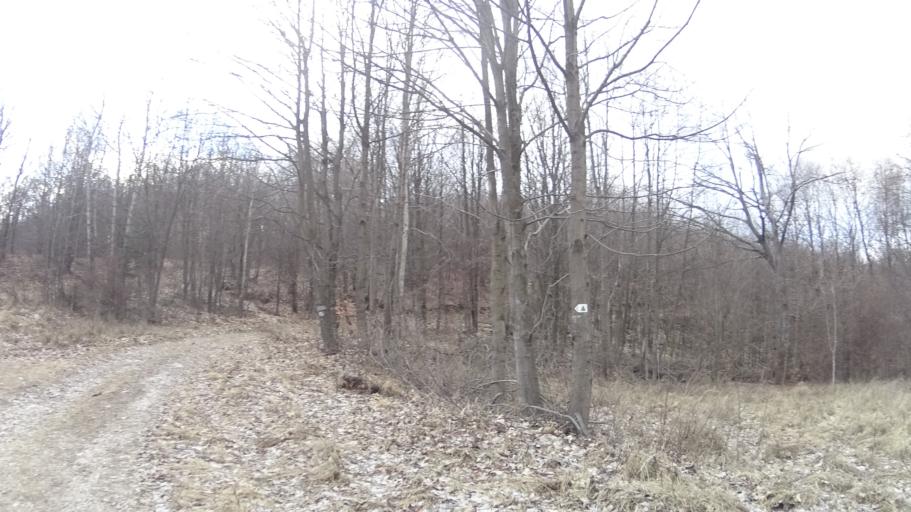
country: HU
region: Heves
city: Szilvasvarad
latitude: 48.0671
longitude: 20.5019
